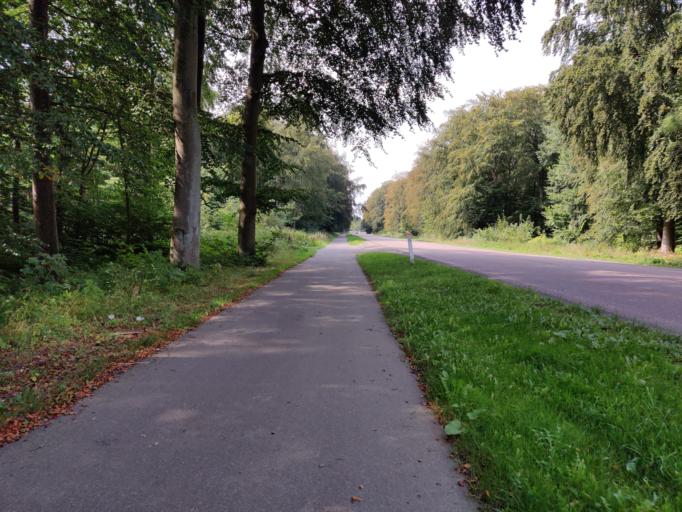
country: DK
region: Zealand
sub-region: Guldborgsund Kommune
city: Nykobing Falster
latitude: 54.7504
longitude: 11.9054
